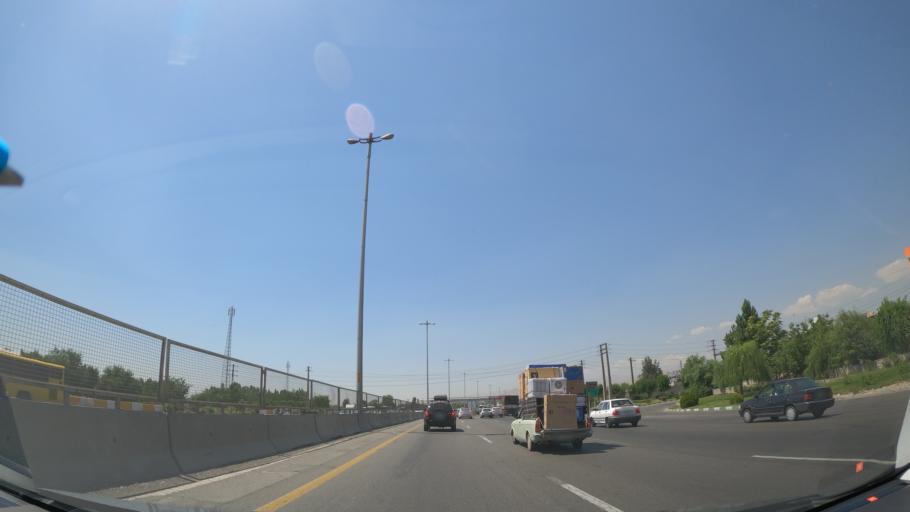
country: IR
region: Alborz
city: Karaj
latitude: 35.8002
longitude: 50.9711
